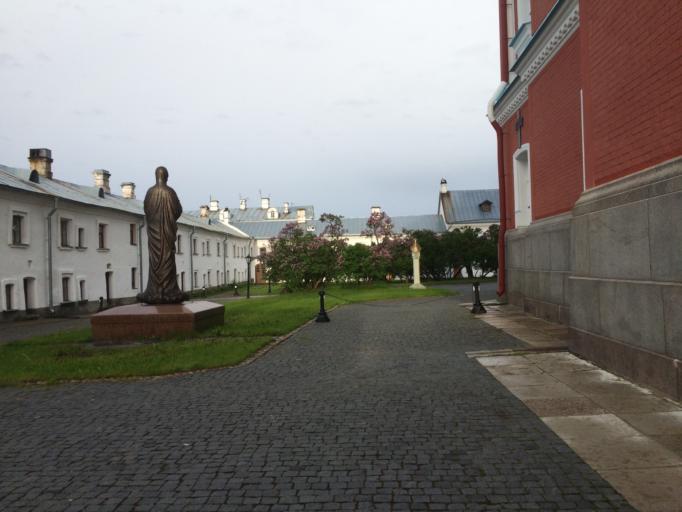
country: RU
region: Republic of Karelia
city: Lyaskelya
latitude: 61.3889
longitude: 30.9459
